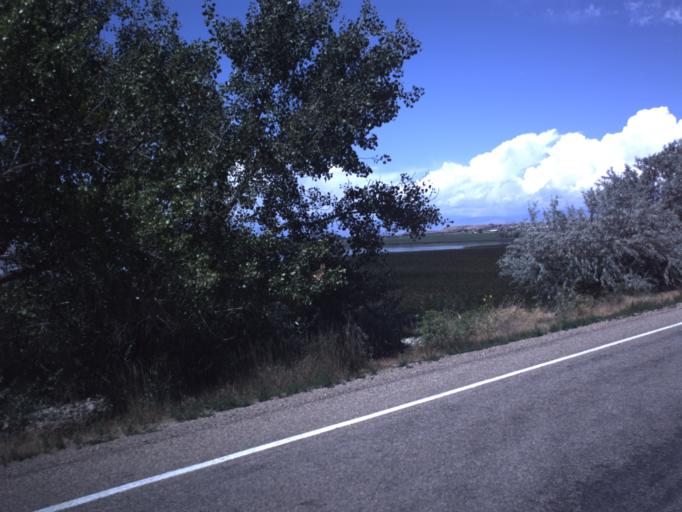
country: US
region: Utah
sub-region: Uintah County
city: Naples
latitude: 40.1890
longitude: -109.6646
